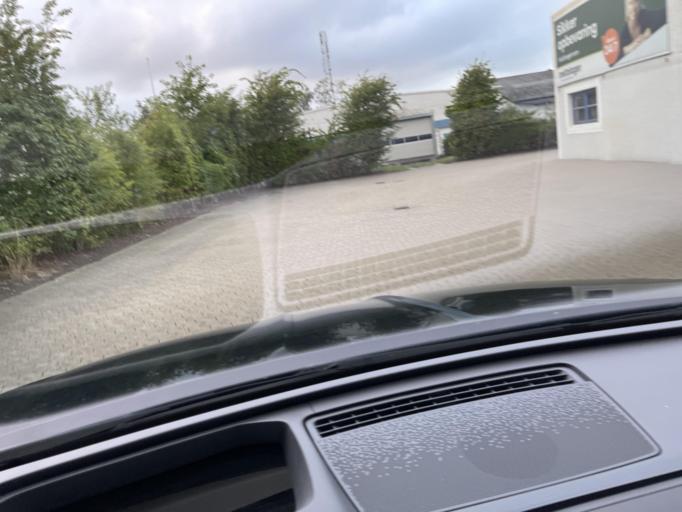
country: DK
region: Zealand
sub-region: Solrod Kommune
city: Havdrup
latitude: 55.5486
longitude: 12.1255
